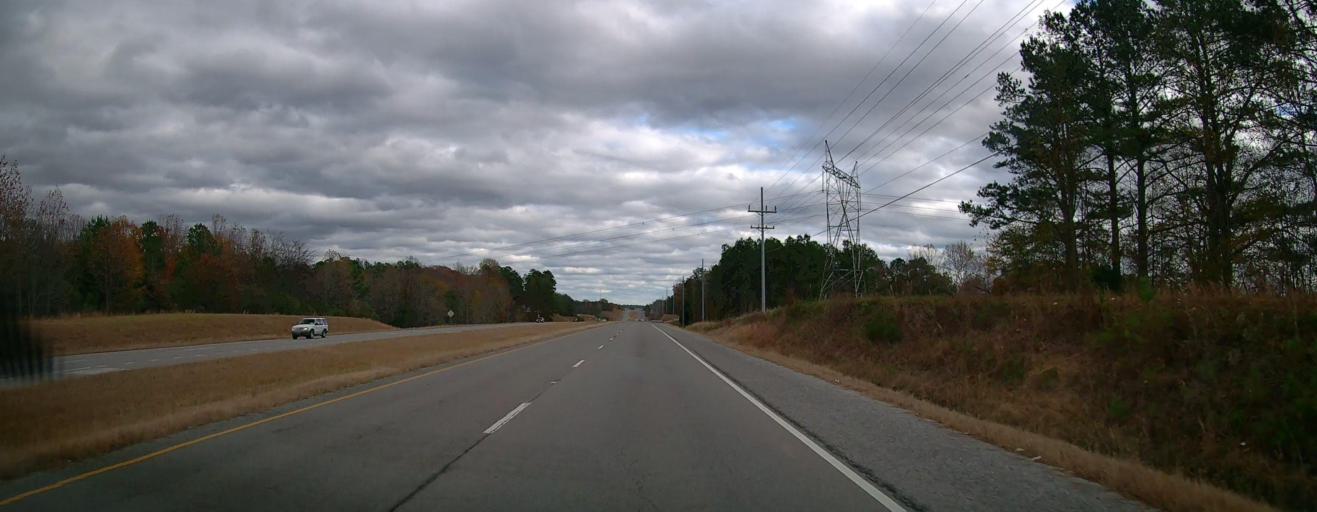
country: US
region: Alabama
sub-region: Lawrence County
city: Moulton
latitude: 34.5669
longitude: -87.3709
